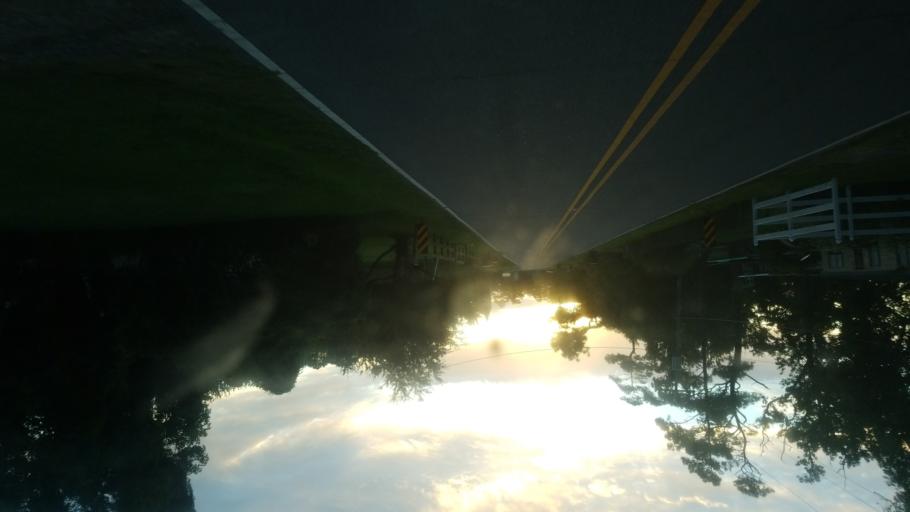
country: US
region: North Carolina
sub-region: Dare County
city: Wanchese
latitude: 35.8426
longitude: -75.6291
